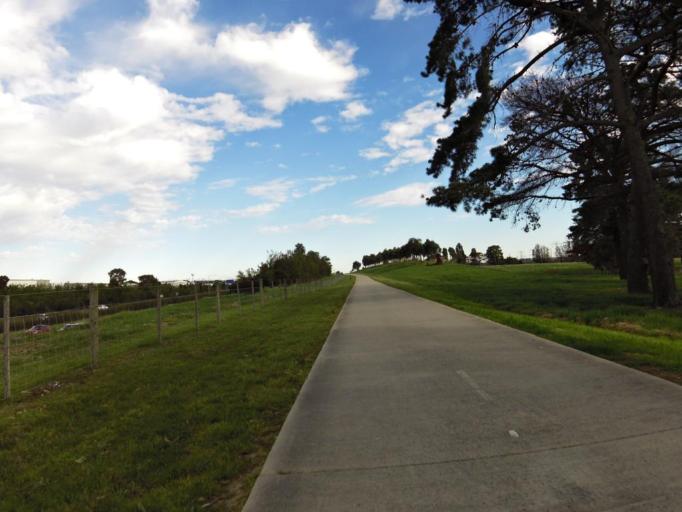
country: AU
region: Victoria
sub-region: Knox
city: Wantirna South
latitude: -37.8950
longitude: 145.2142
